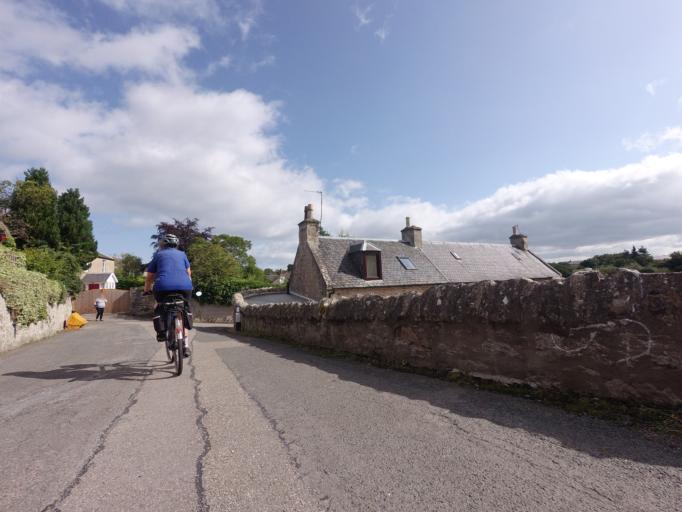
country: GB
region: Scotland
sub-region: Highland
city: Nairn
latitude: 57.5829
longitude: -3.8675
